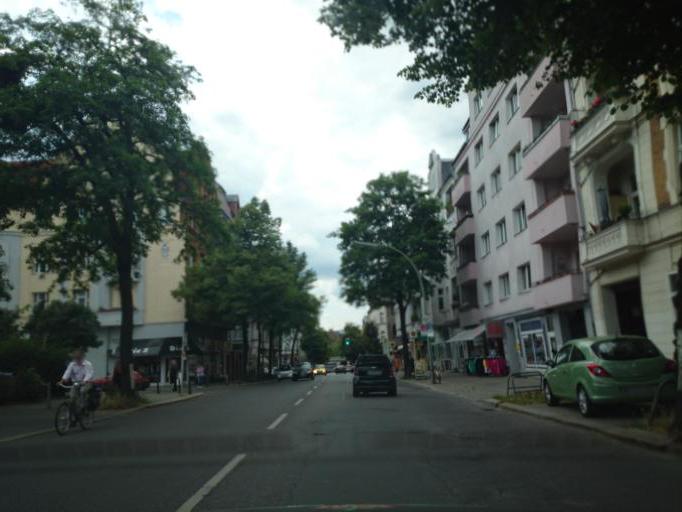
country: DE
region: Berlin
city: Steglitz Bezirk
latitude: 52.4549
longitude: 13.3269
